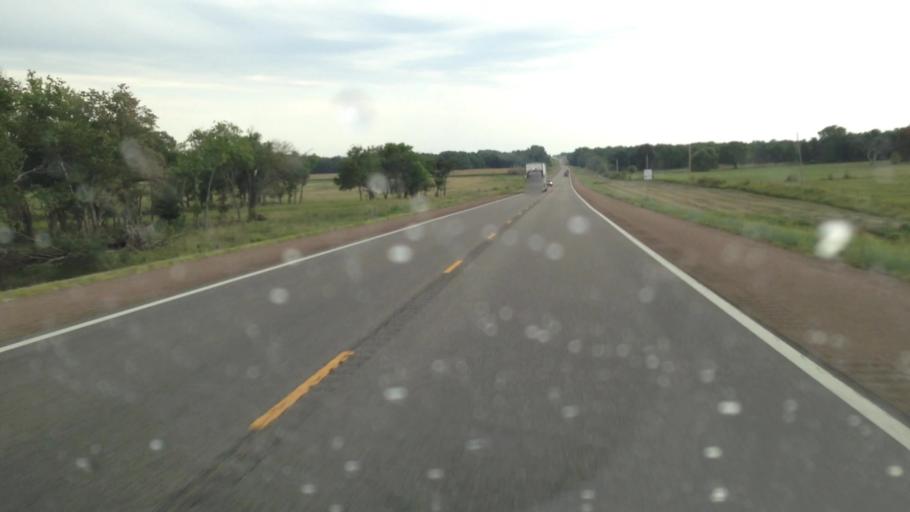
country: US
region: Kansas
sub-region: Coffey County
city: Burlington
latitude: 38.0378
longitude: -95.7389
